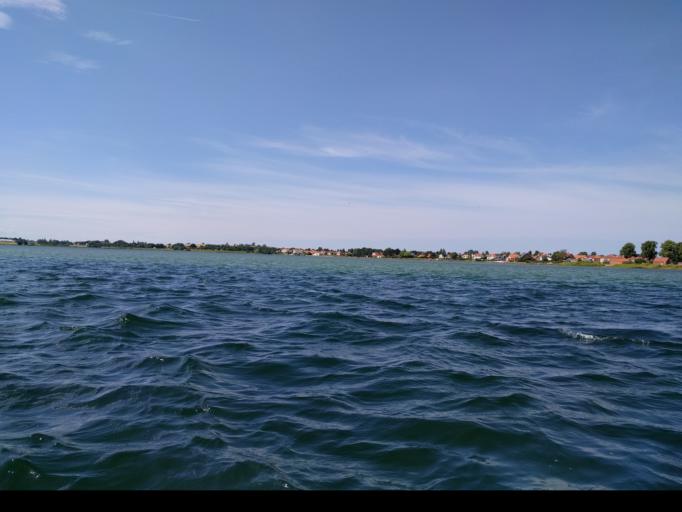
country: DK
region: South Denmark
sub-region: Kerteminde Kommune
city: Kerteminde
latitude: 55.4445
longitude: 10.6503
